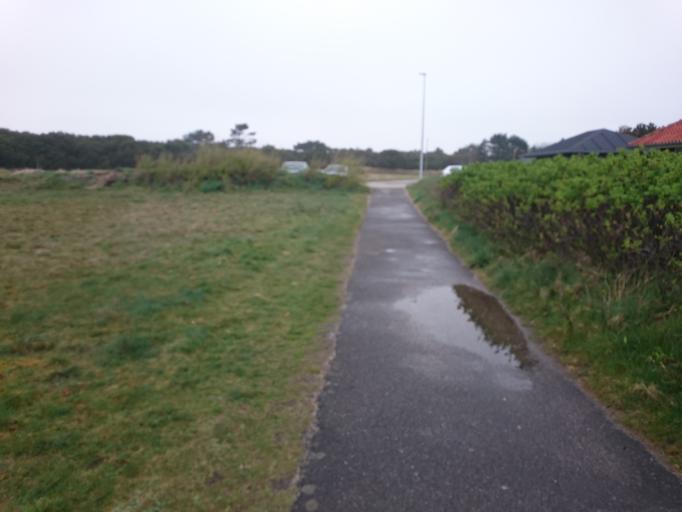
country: DK
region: South Denmark
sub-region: Fano Kommune
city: Nordby
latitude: 55.4479
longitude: 8.3955
